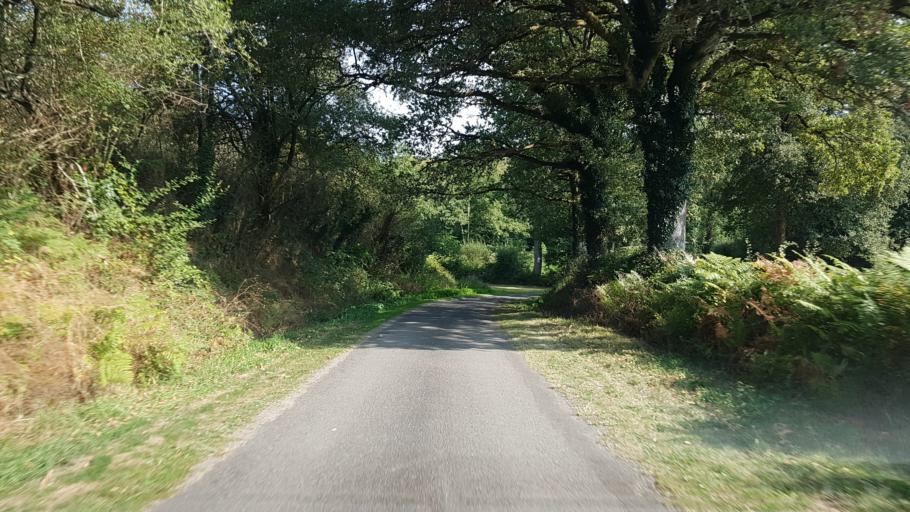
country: FR
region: Poitou-Charentes
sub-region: Departement de la Charente
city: Etagnac
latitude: 45.9094
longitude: 0.7781
